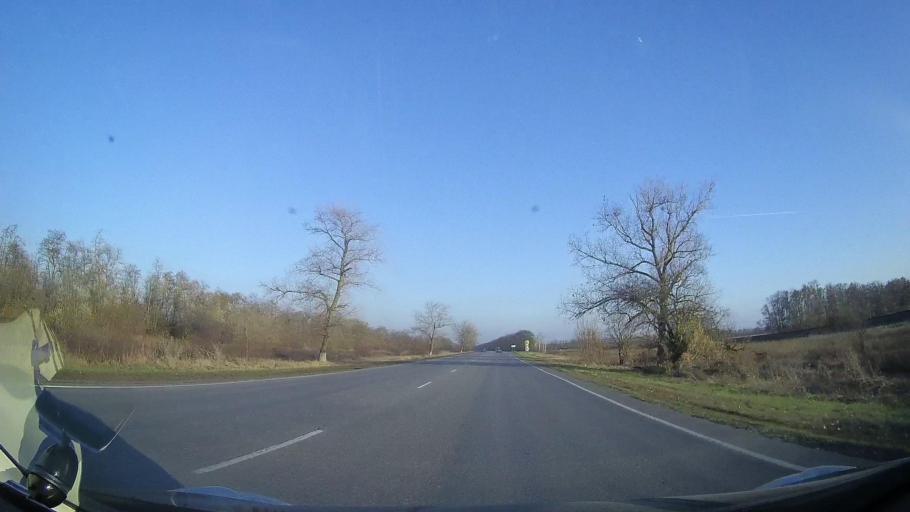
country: RU
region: Rostov
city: Kirovskaya
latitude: 47.0073
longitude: 39.9517
